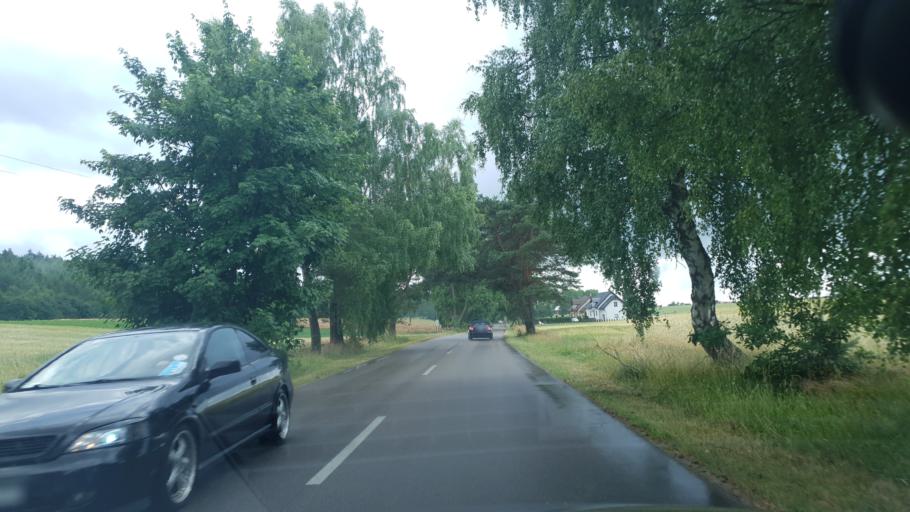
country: PL
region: Pomeranian Voivodeship
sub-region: Powiat kartuski
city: Stezyca
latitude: 54.2451
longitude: 17.9988
